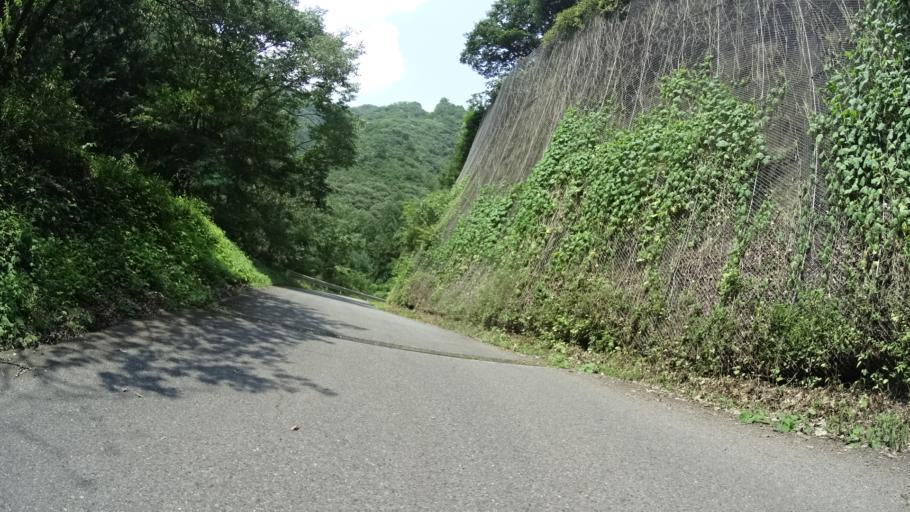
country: JP
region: Gunma
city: Tomioka
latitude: 36.0816
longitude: 138.7090
